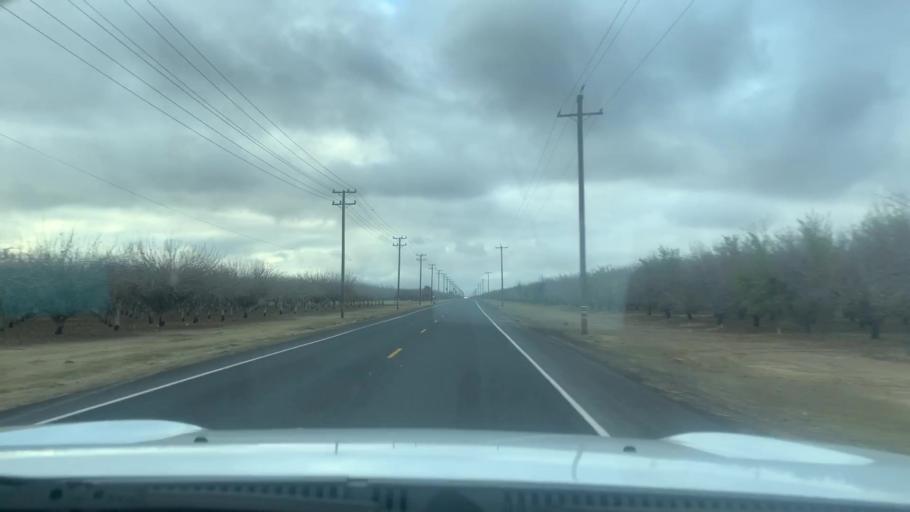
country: US
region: California
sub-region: Kern County
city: Lost Hills
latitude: 35.4993
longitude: -119.6550
